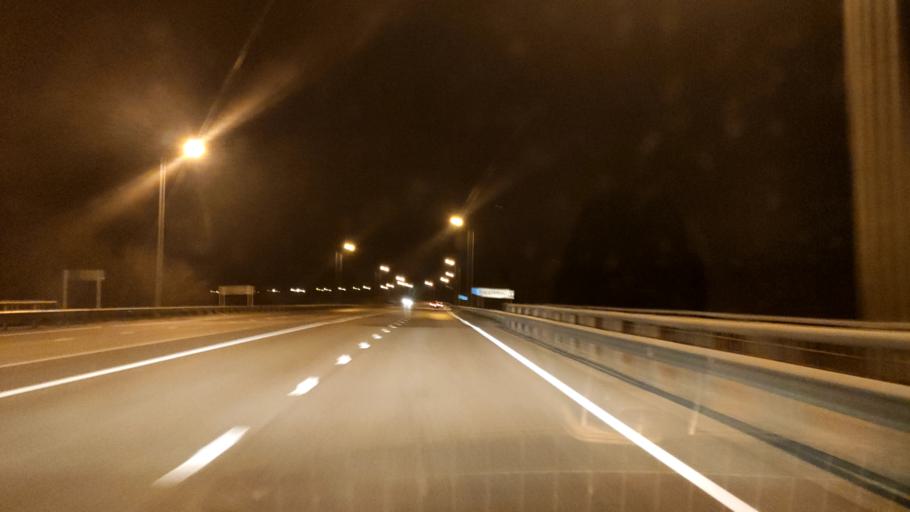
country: RU
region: Belgorod
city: Staryy Oskol
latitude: 51.3451
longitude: 37.8164
